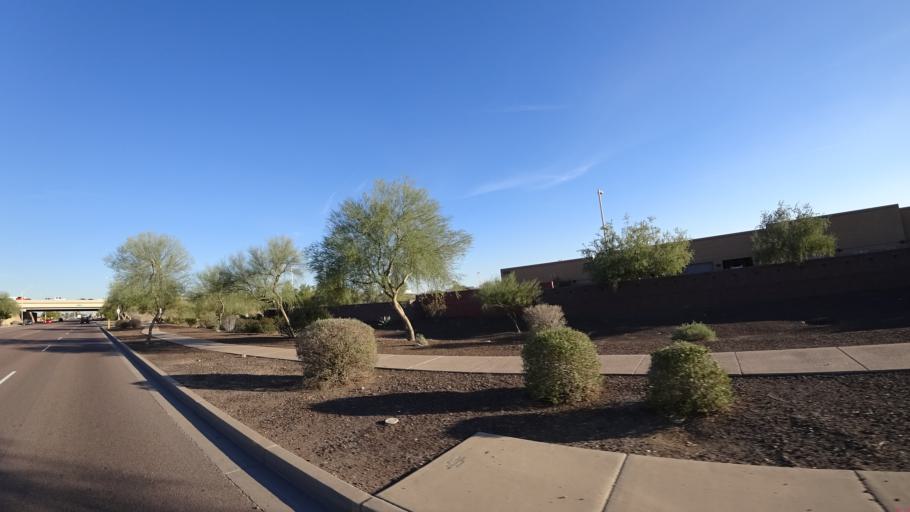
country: US
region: Arizona
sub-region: Maricopa County
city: Phoenix
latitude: 33.4313
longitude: -112.0399
